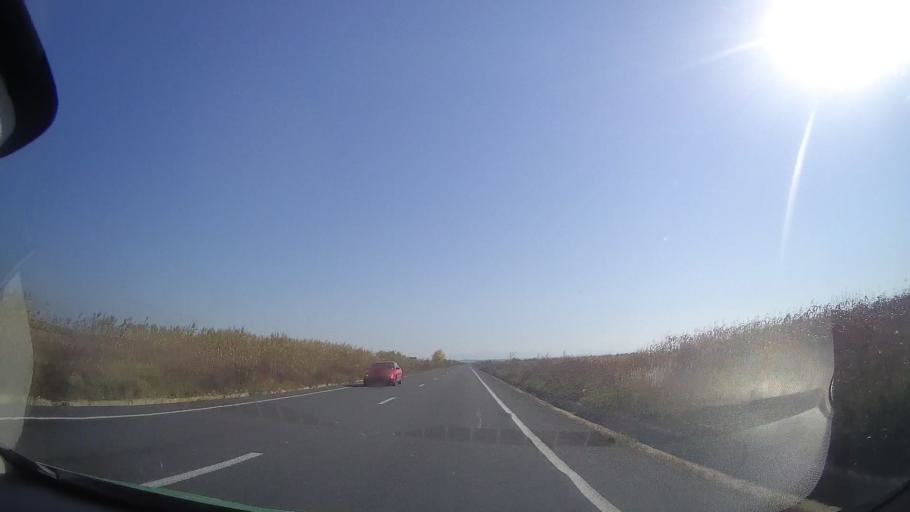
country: RO
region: Timis
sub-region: Comuna Costeiu
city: Costeiu
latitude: 45.7449
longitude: 21.8052
